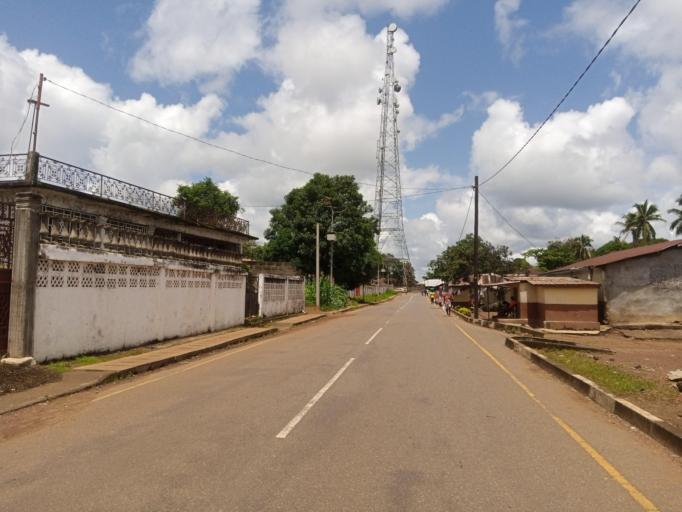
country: SL
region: Northern Province
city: Port Loko
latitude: 8.7668
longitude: -12.7878
